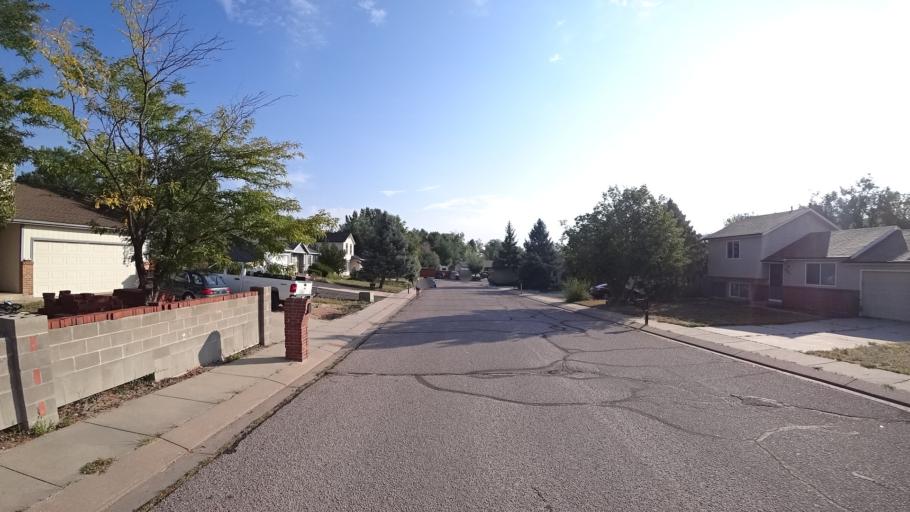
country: US
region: Colorado
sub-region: El Paso County
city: Colorado Springs
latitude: 38.8831
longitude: -104.7935
